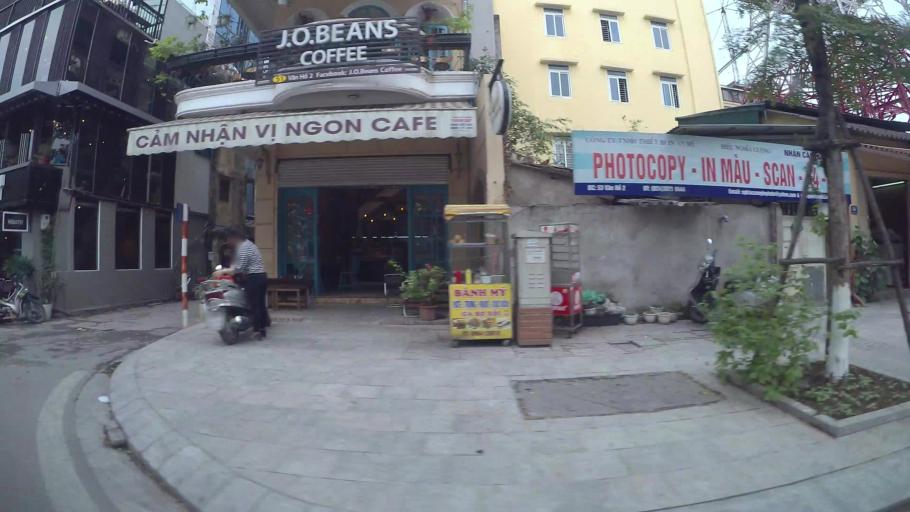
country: VN
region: Ha Noi
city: Hai BaTrung
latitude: 21.0113
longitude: 105.8460
